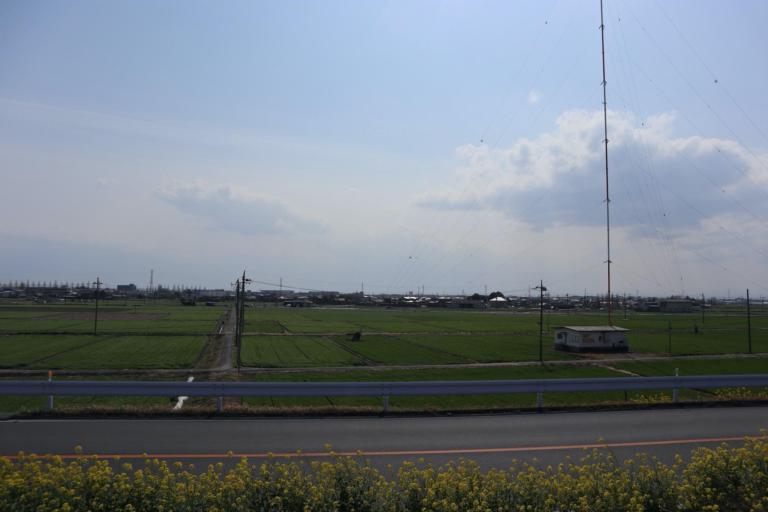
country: JP
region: Tochigi
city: Ashikaga
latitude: 36.3021
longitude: 139.4947
